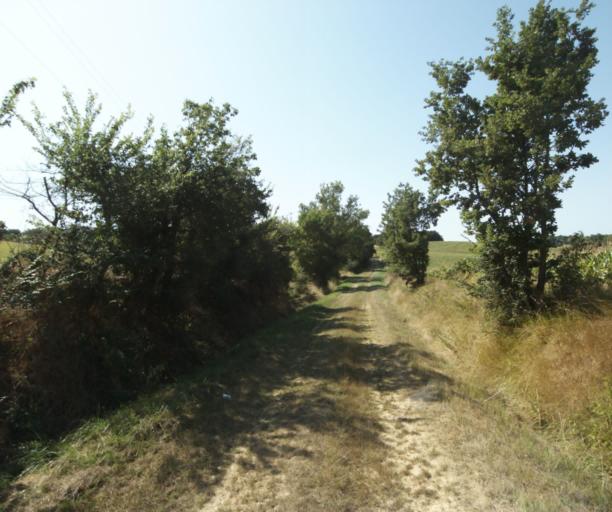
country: FR
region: Midi-Pyrenees
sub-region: Departement de la Haute-Garonne
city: Saint-Felix-Lauragais
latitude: 43.4552
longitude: 1.8617
